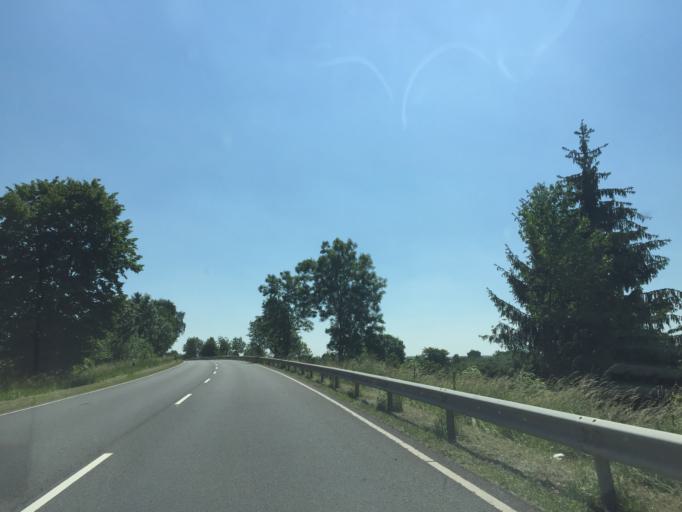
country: DE
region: Baden-Wuerttemberg
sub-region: Karlsruhe Region
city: Walldurn
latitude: 49.5849
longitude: 9.3720
